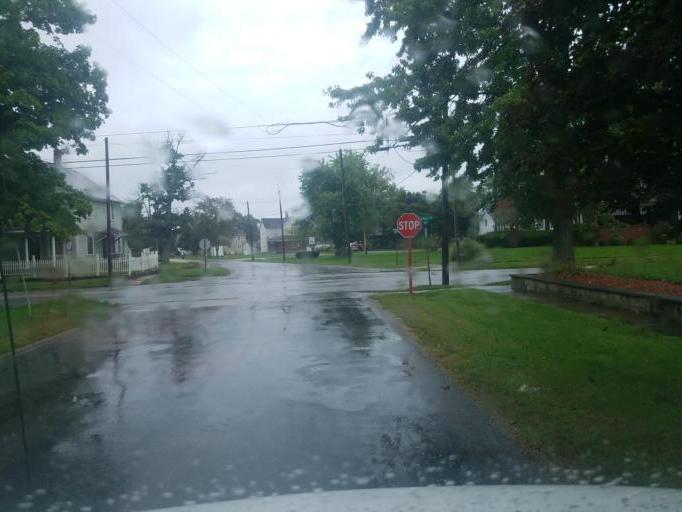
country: US
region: Ohio
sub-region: Wayne County
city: Creston
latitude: 40.9869
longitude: -81.8931
